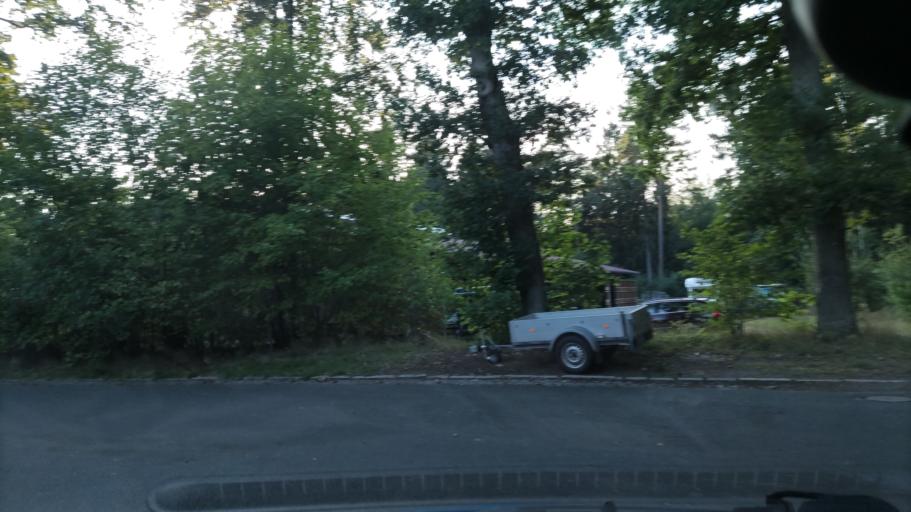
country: DE
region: Lower Saxony
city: Fassberg
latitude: 52.9633
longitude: 10.1858
